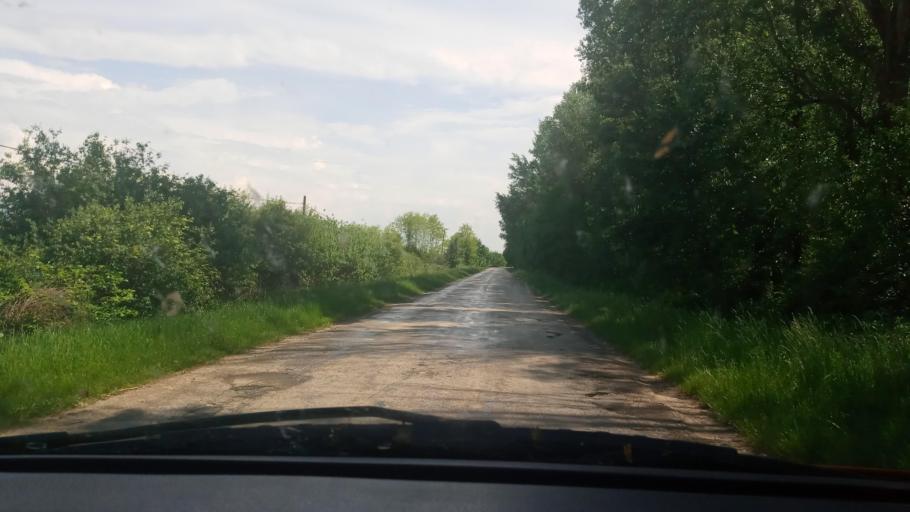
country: HU
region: Baranya
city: Siklos
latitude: 45.7998
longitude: 18.3479
